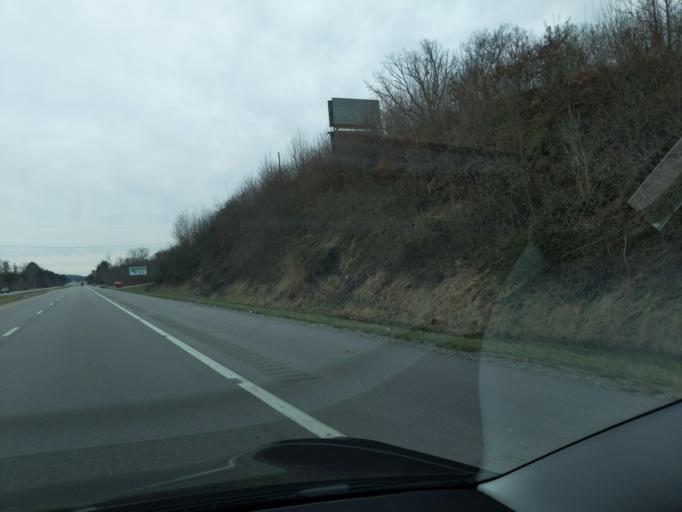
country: US
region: Kentucky
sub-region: Laurel County
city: North Corbin
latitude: 36.9445
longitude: -84.0204
